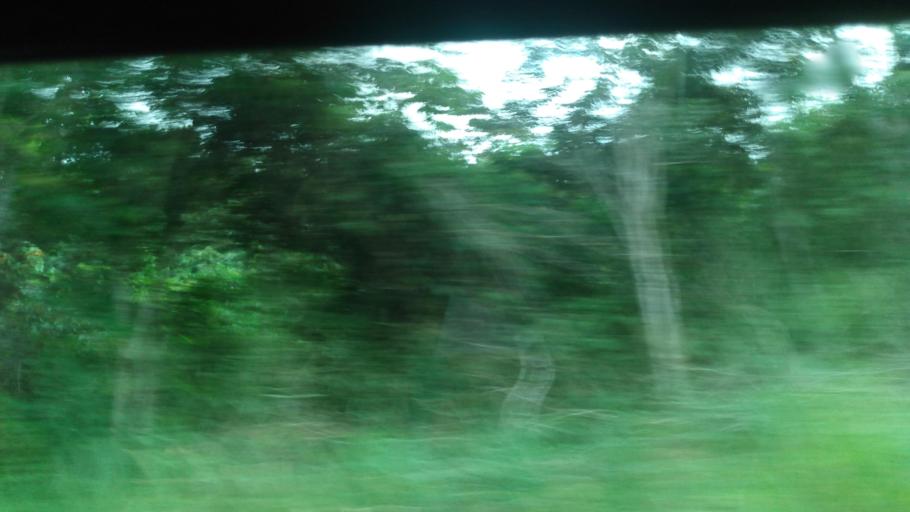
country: BR
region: Pernambuco
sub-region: Maraial
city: Maraial
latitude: -8.7851
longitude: -35.9073
